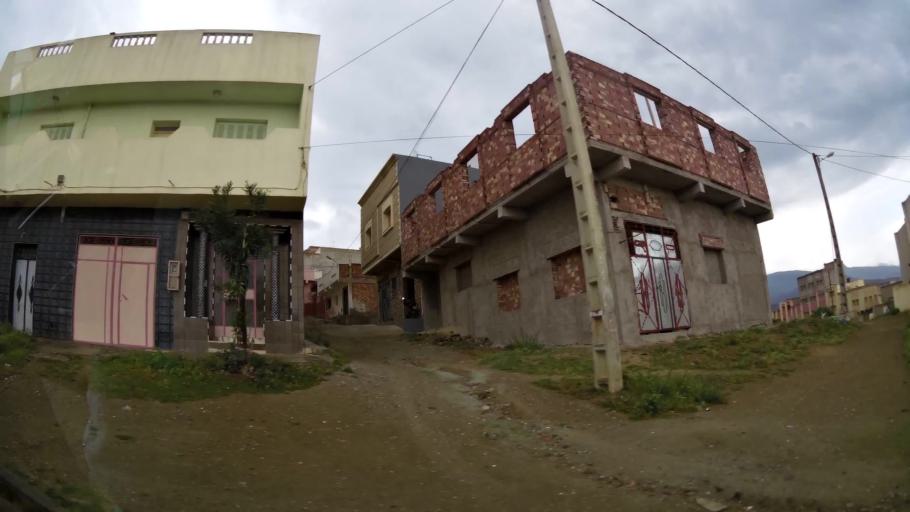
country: MA
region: Oriental
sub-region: Nador
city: Nador
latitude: 35.1468
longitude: -3.0001
